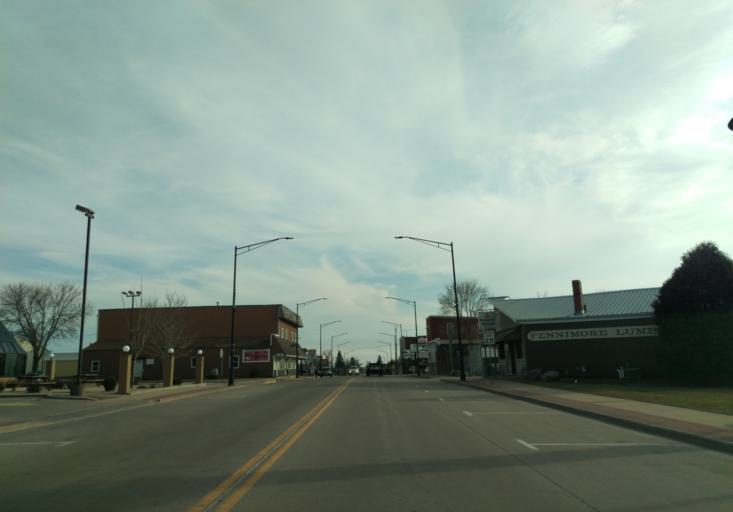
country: US
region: Wisconsin
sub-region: Grant County
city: Fennimore
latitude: 42.9862
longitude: -90.6556
